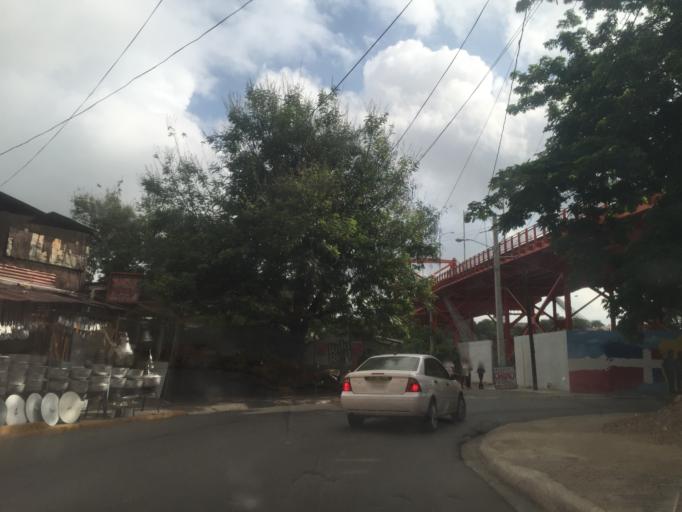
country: DO
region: Santiago
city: Santiago de los Caballeros
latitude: 19.4462
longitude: -70.7092
